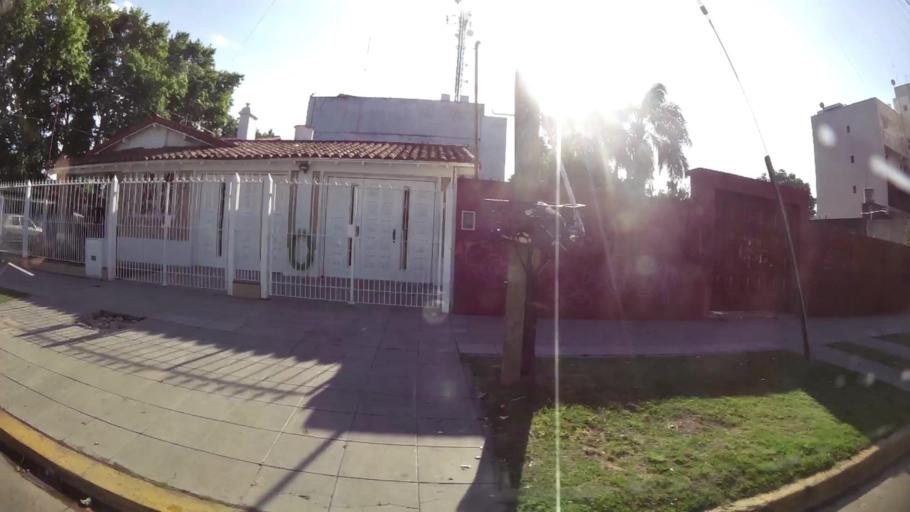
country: AR
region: Buenos Aires
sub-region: Partido de Merlo
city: Merlo
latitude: -34.6669
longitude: -58.7245
